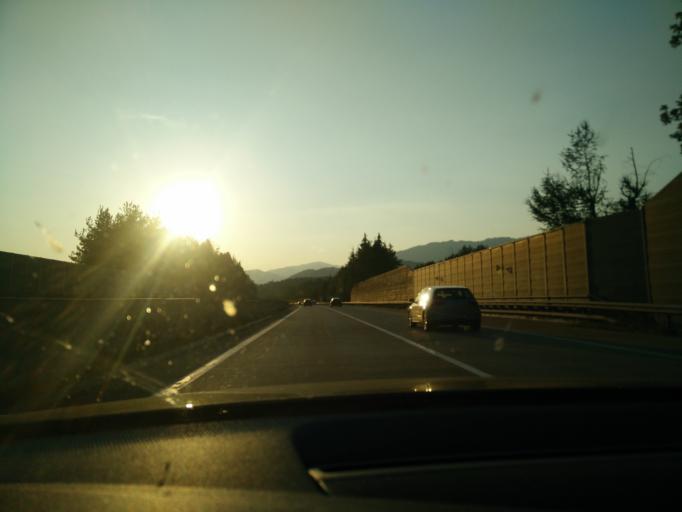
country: AT
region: Carinthia
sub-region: Politischer Bezirk Villach Land
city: Wernberg
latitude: 46.6214
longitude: 13.9776
